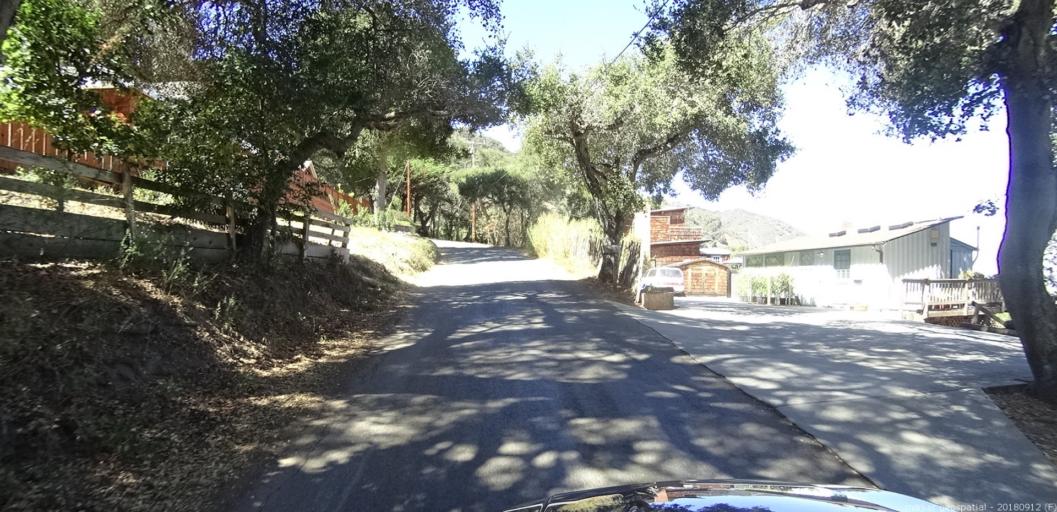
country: US
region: California
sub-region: Monterey County
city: Carmel Valley Village
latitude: 36.4718
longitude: -121.7343
